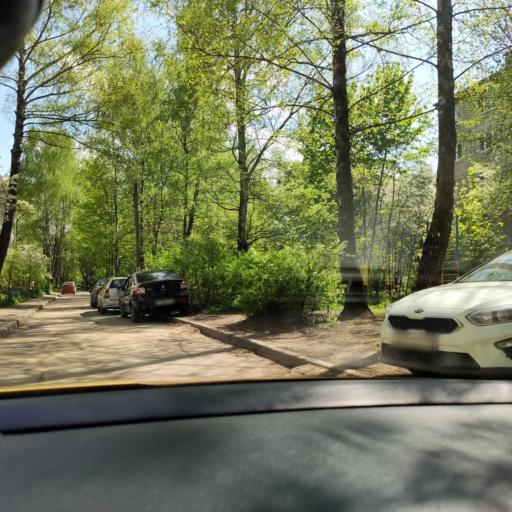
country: RU
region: Moskovskaya
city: Dolgoprudnyy
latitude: 55.9474
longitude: 37.5134
